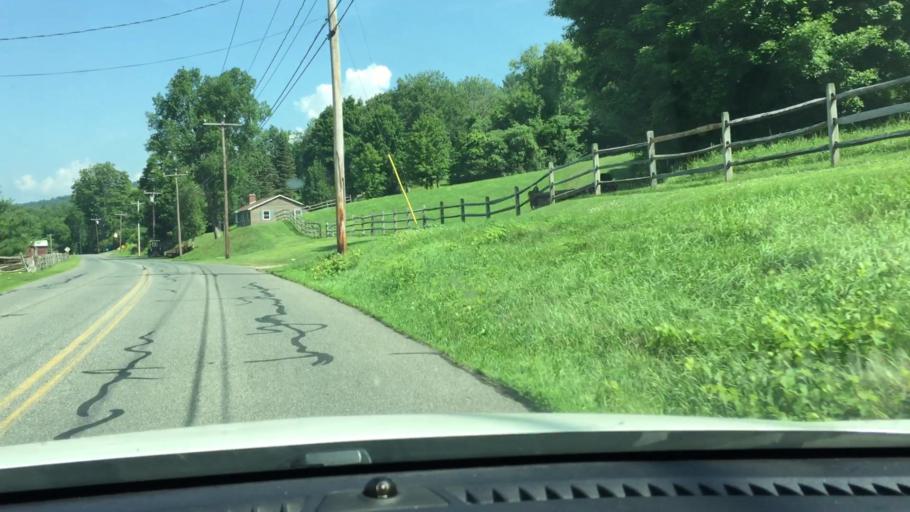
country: US
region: Massachusetts
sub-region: Berkshire County
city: Lee
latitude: 42.2383
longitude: -73.1950
